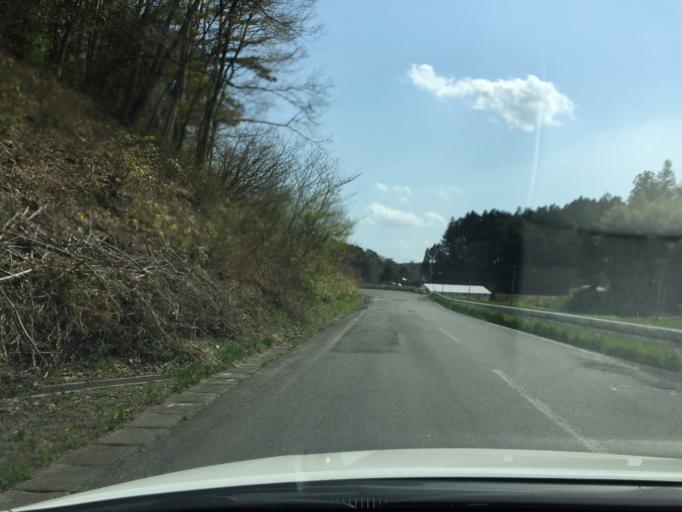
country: JP
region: Fukushima
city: Namie
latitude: 37.3985
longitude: 140.8017
